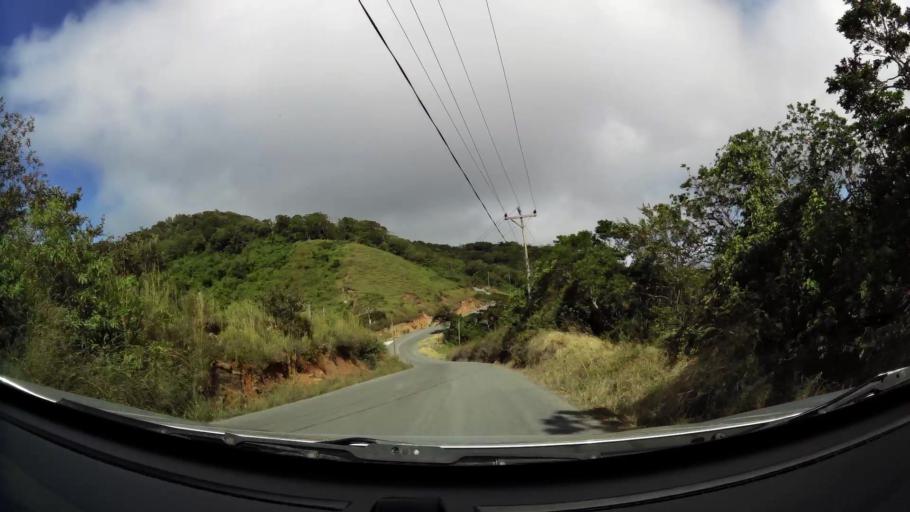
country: CR
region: Guanacaste
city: Juntas
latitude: 10.3453
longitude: -84.9063
